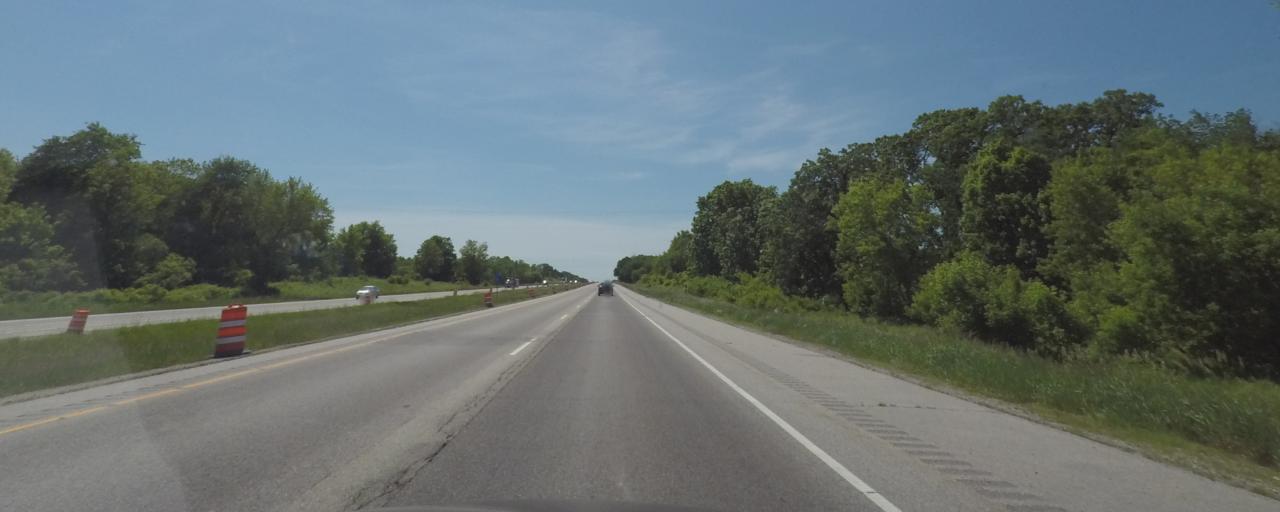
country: US
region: Wisconsin
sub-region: Jefferson County
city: Waterloo
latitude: 43.1110
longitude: -88.9917
